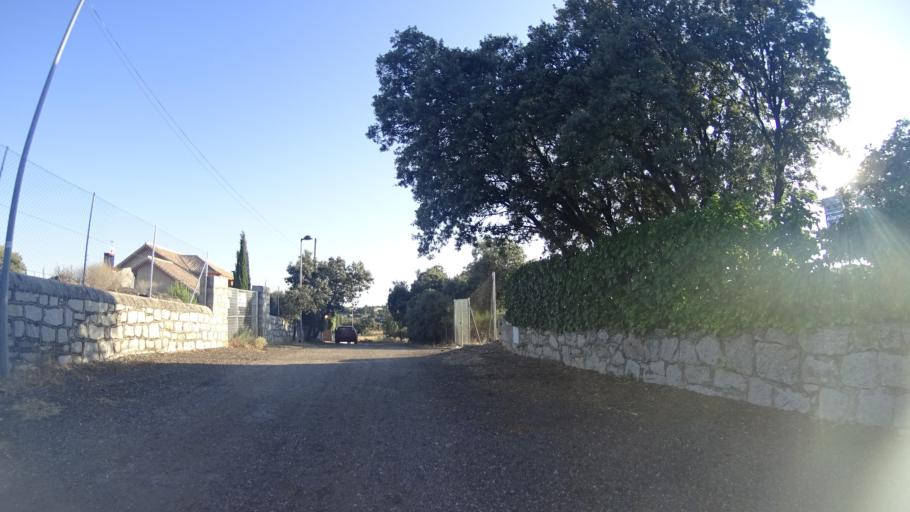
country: ES
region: Madrid
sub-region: Provincia de Madrid
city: Galapagar
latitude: 40.5633
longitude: -4.0022
